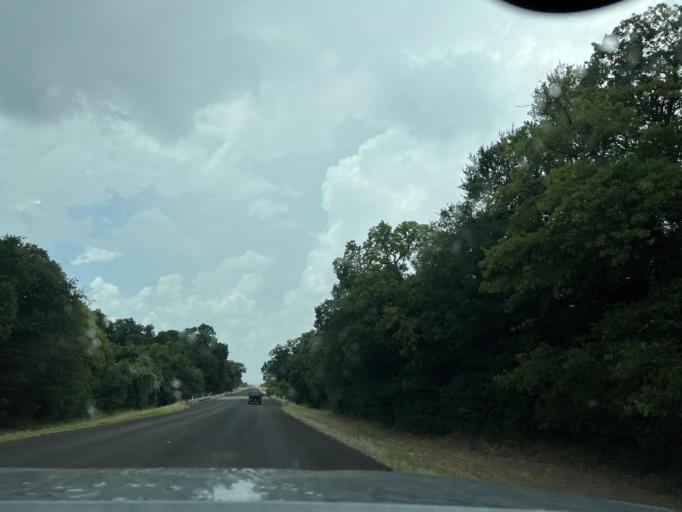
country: US
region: Texas
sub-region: Wise County
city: Decatur
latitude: 33.1508
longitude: -97.6354
